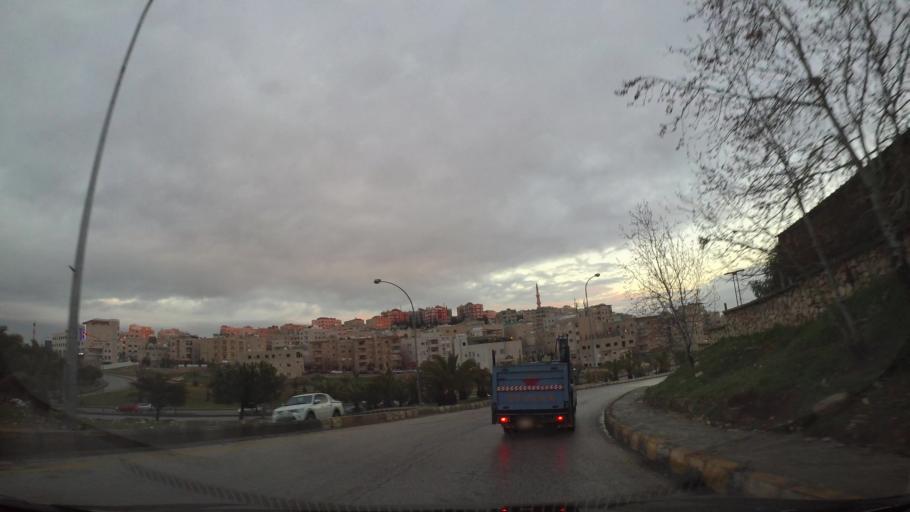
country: JO
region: Amman
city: Amman
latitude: 31.9922
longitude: 35.9175
